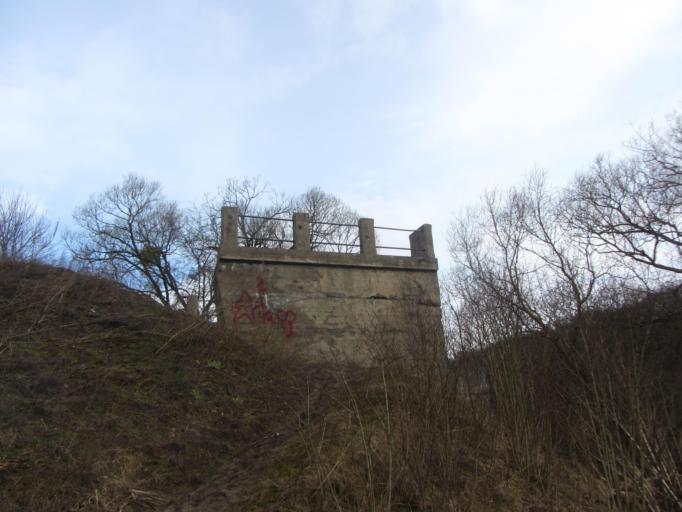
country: LT
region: Kauno apskritis
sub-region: Kauno rajonas
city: Akademija (Kaunas)
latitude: 54.9336
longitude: 23.7930
